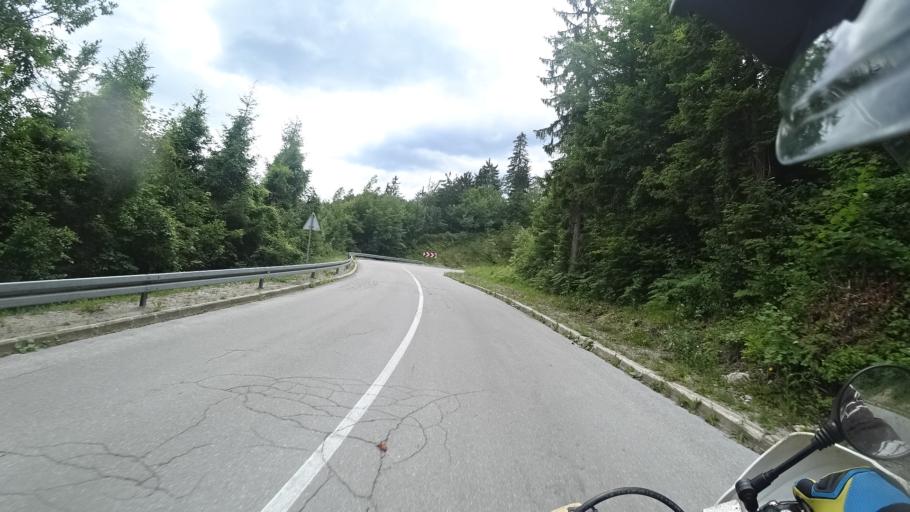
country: SI
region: Osilnica
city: Osilnica
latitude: 45.5959
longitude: 14.6366
